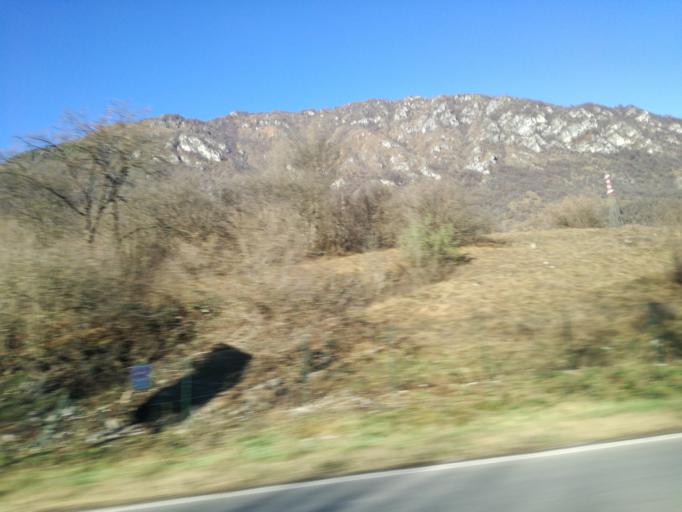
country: IT
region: Lombardy
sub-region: Provincia di Bergamo
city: Piangaiano
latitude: 45.7977
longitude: 10.0126
